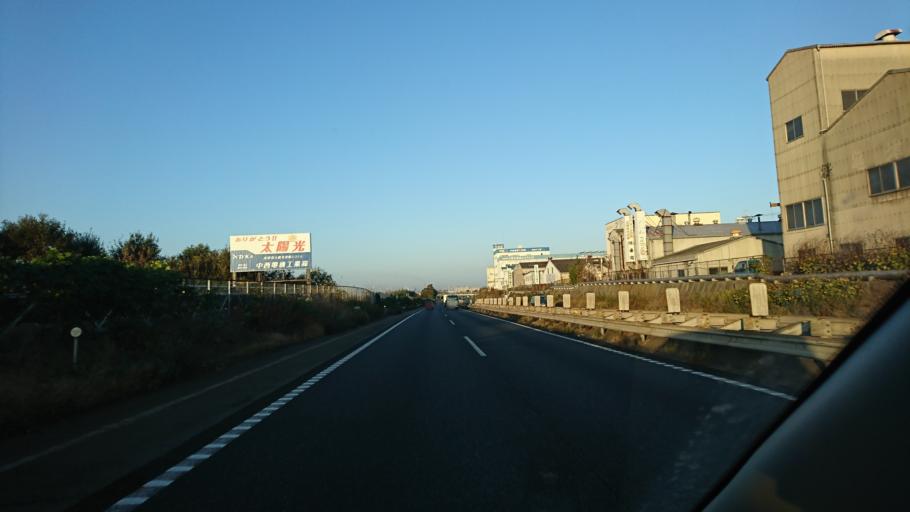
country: JP
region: Hyogo
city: Akashi
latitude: 34.7157
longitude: 134.9238
